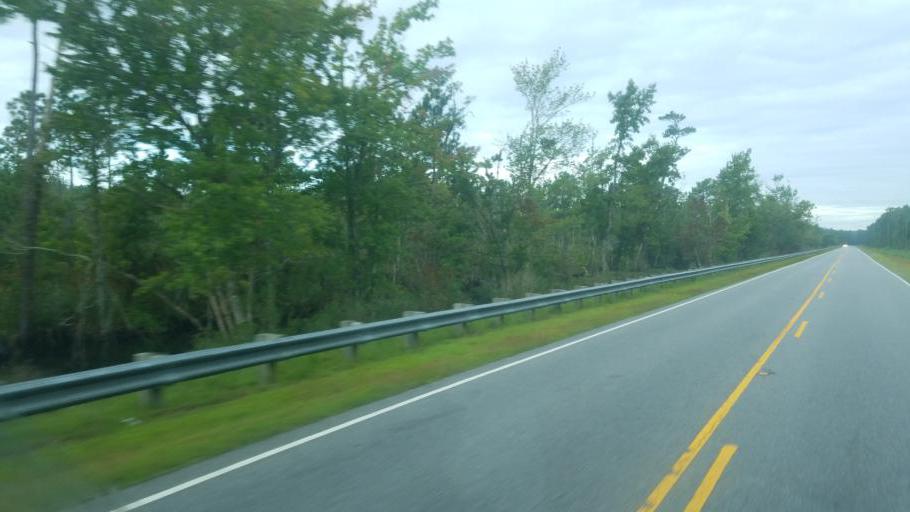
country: US
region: North Carolina
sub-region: Dare County
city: Manteo
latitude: 35.8704
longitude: -75.9022
